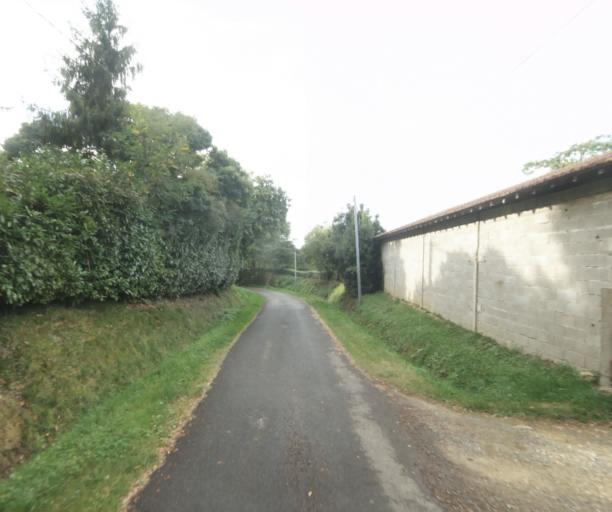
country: FR
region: Midi-Pyrenees
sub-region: Departement du Gers
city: Cazaubon
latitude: 43.8718
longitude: -0.1160
